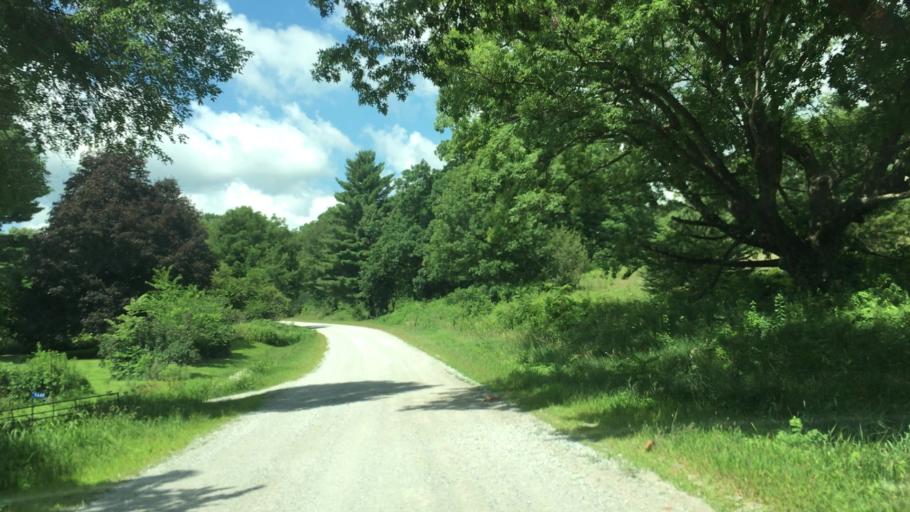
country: US
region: Iowa
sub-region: Linn County
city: Lisbon
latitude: 41.8286
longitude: -91.3804
